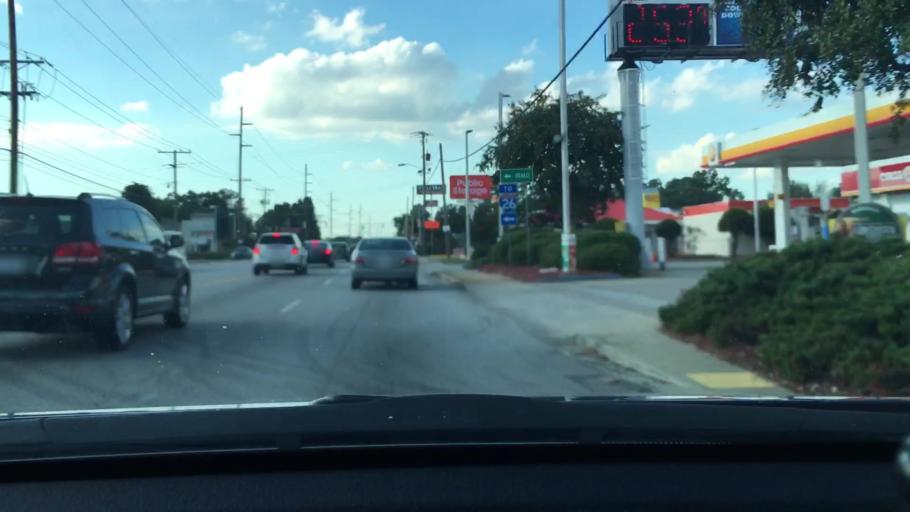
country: US
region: South Carolina
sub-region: Lexington County
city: Saint Andrews
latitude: 34.0487
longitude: -81.1042
